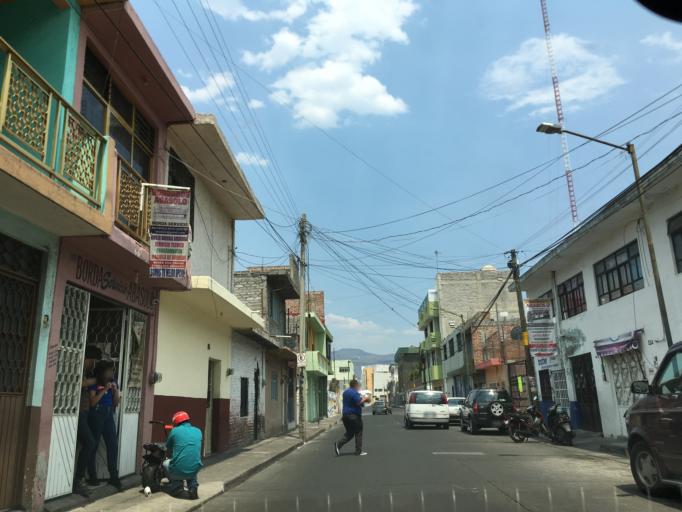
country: MX
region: Guanajuato
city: Uriangato
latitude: 20.1316
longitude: -101.1836
